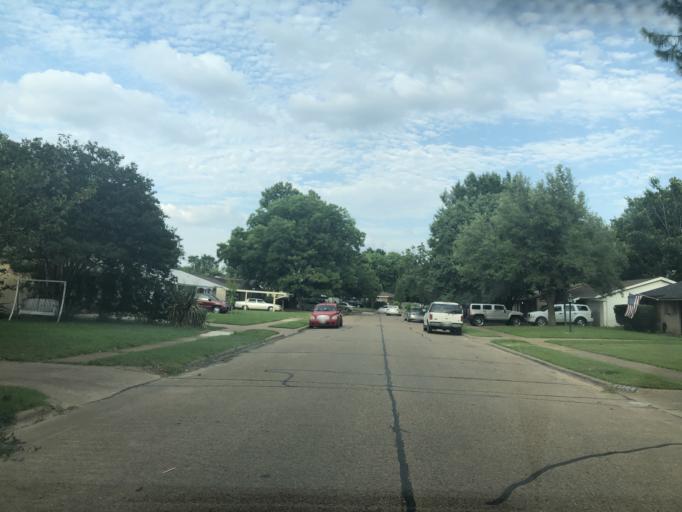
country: US
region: Texas
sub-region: Dallas County
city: Irving
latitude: 32.7883
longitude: -96.9757
